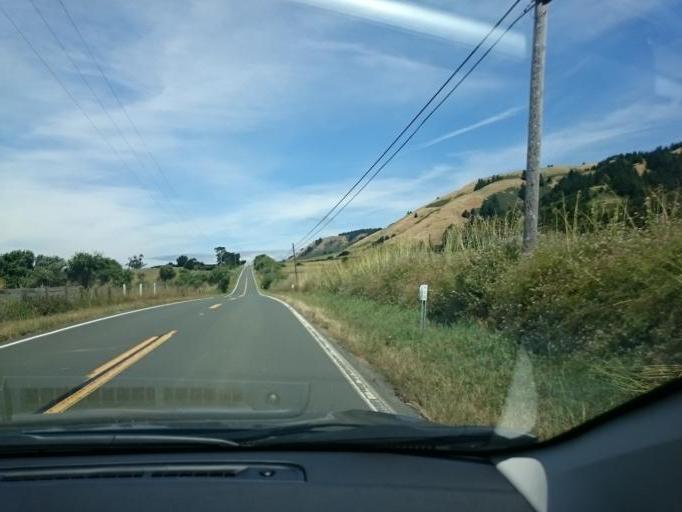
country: US
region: California
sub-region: Mendocino County
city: Boonville
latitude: 39.0600
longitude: -123.6872
